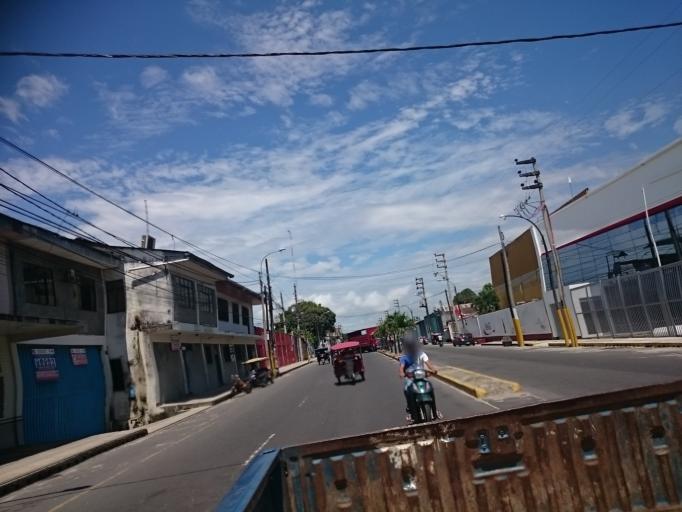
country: PE
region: Loreto
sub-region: Provincia de Maynas
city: Iquitos
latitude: -3.7368
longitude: -73.2409
